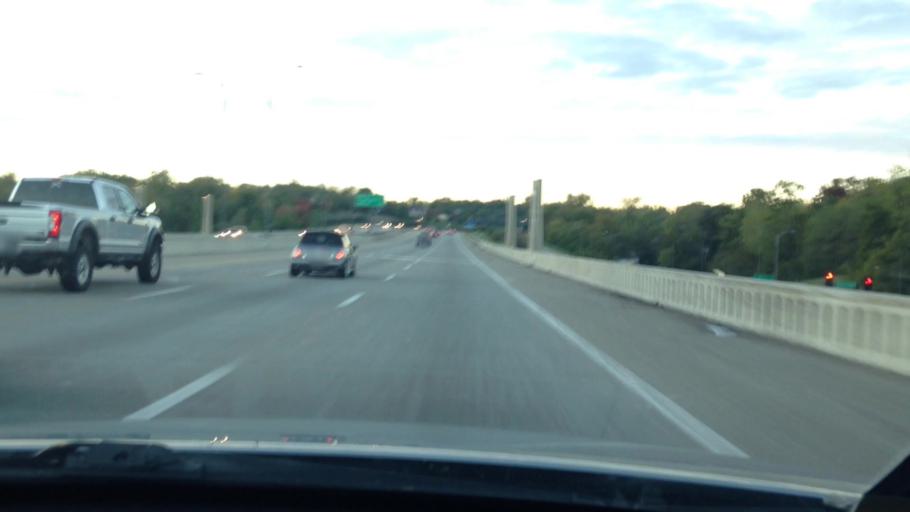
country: US
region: Kansas
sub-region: Johnson County
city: Westwood
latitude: 39.0420
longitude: -94.5594
